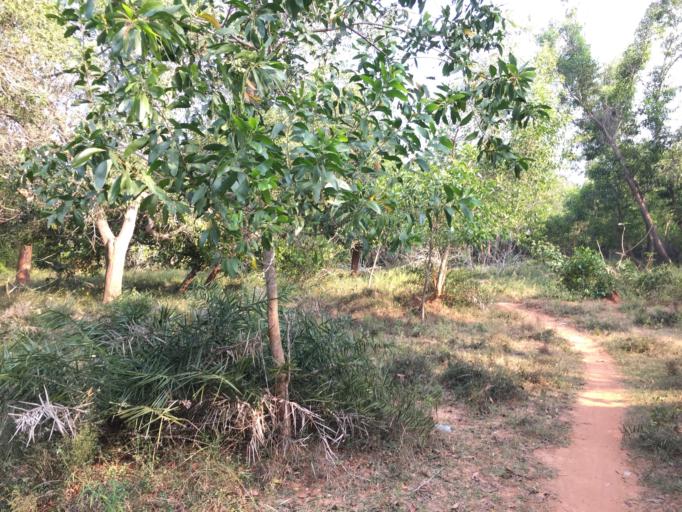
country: IN
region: Tamil Nadu
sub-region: Villupuram
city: Auroville
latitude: 11.9986
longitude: 79.8076
